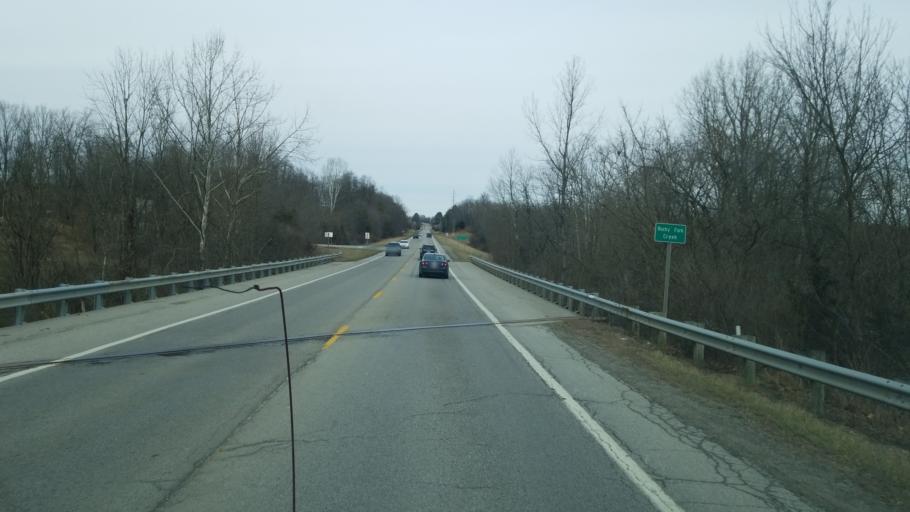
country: US
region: Ohio
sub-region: Highland County
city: Hillsboro
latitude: 39.1750
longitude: -83.6221
